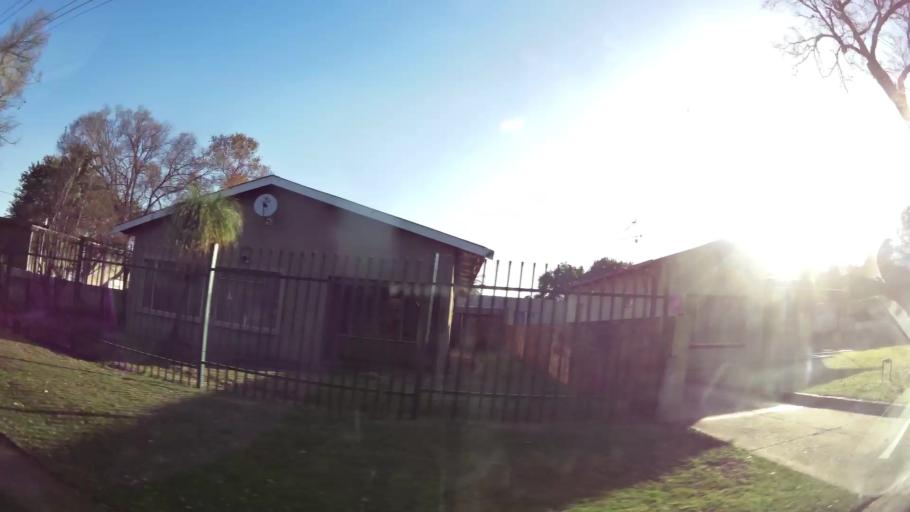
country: ZA
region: Gauteng
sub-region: City of Tshwane Metropolitan Municipality
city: Pretoria
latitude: -25.7016
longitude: 28.2044
